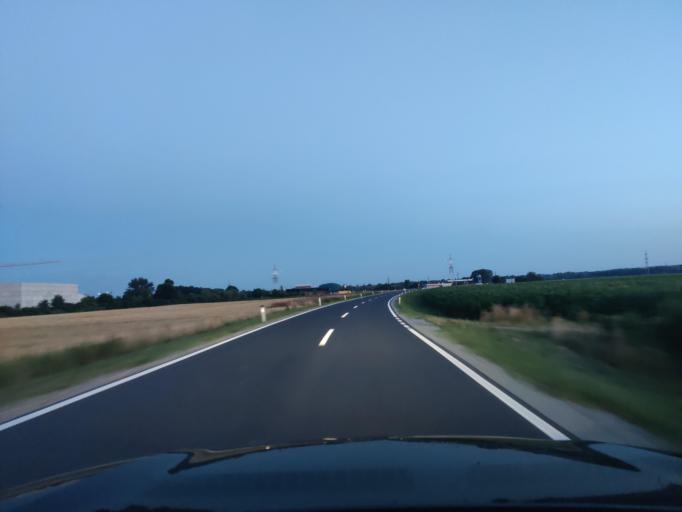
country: SI
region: Lendava-Lendva
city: Lendava
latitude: 46.5464
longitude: 16.4441
